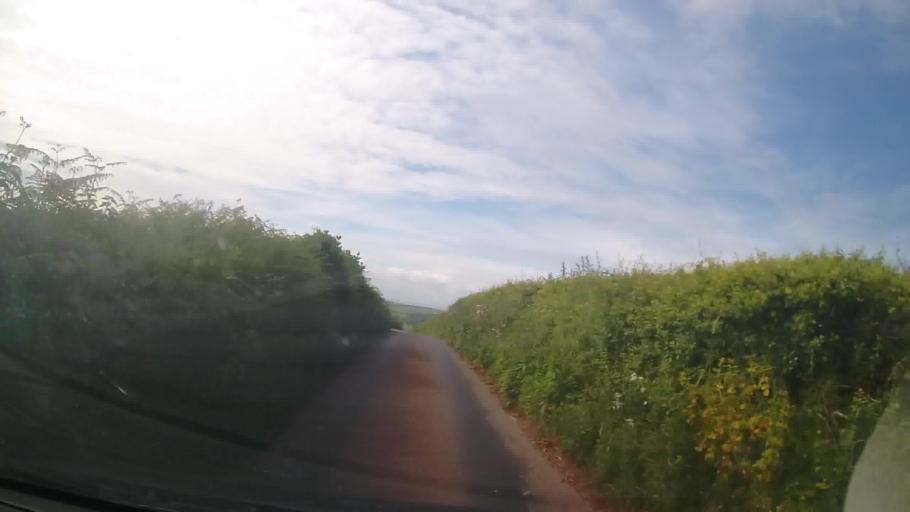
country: GB
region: England
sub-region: Devon
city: Salcombe
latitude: 50.2334
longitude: -3.6716
